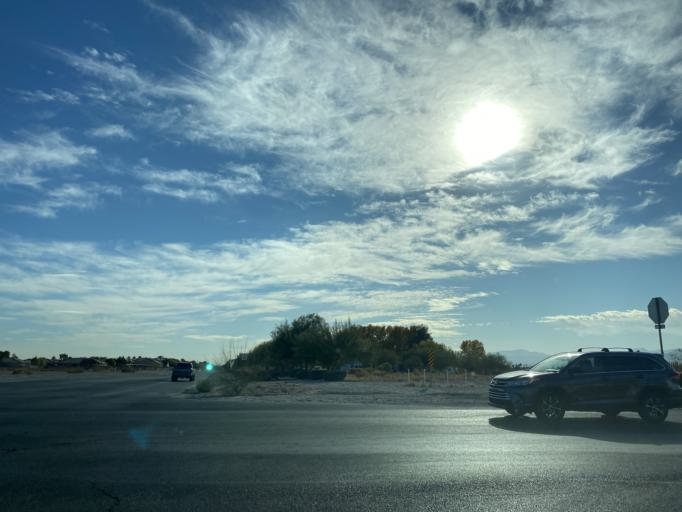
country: US
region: Nevada
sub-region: Clark County
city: North Las Vegas
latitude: 36.3054
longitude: -115.2422
